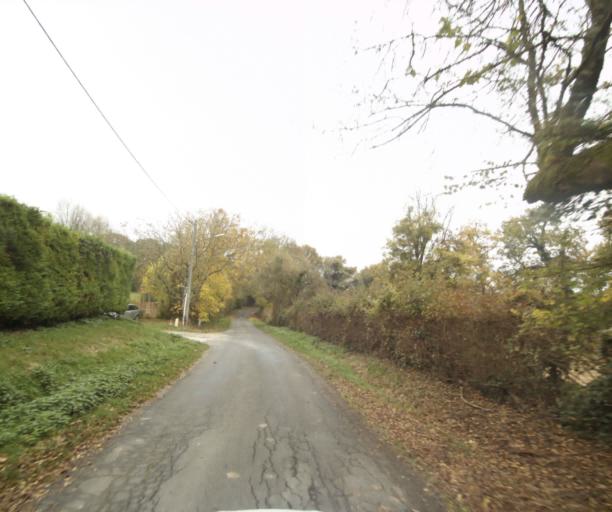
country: FR
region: Poitou-Charentes
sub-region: Departement de la Charente-Maritime
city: Saint-Georges-des-Coteaux
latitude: 45.7400
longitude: -0.6904
